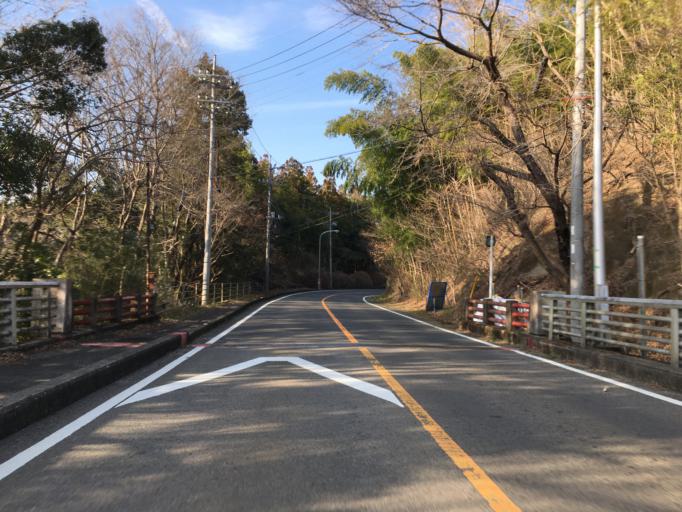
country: JP
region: Ibaraki
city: Daigo
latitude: 36.7563
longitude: 140.3899
